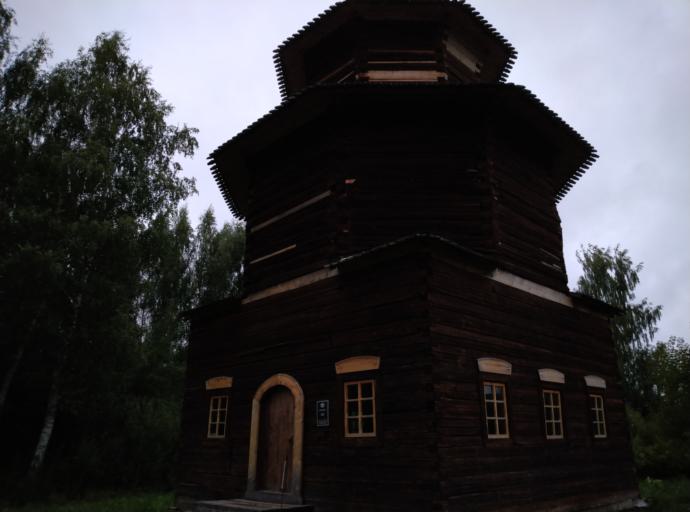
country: RU
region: Kostroma
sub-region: Kostromskoy Rayon
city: Kostroma
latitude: 57.7731
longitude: 40.8923
